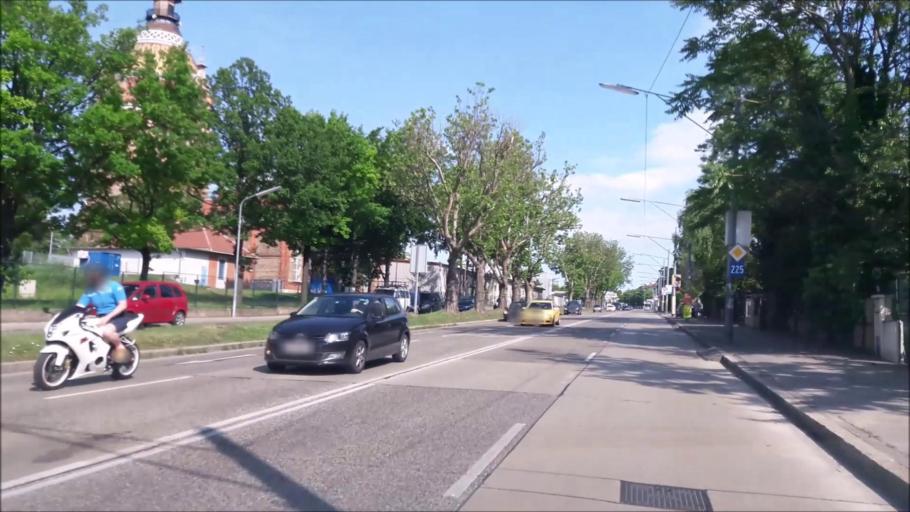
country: AT
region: Vienna
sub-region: Wien Stadt
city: Vienna
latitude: 48.1691
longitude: 16.3514
